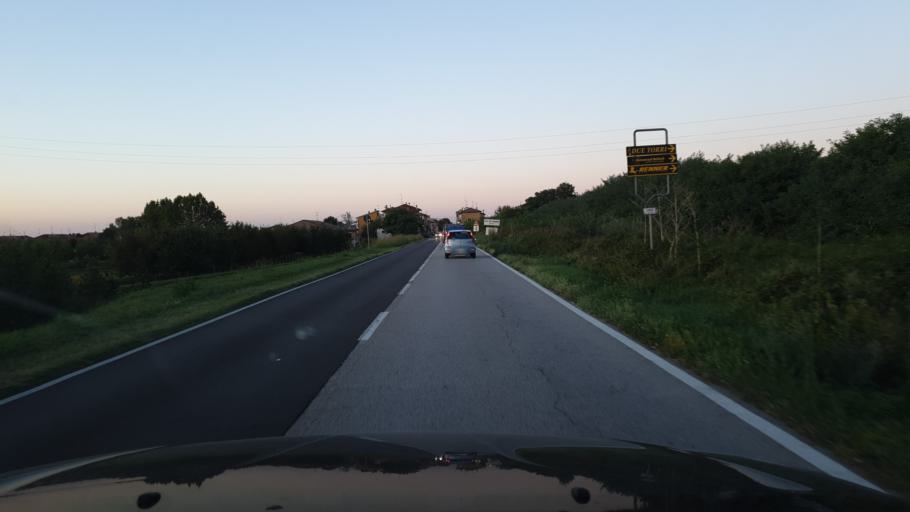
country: IT
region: Emilia-Romagna
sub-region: Provincia di Bologna
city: Ca De Fabbri
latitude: 44.6163
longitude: 11.4515
